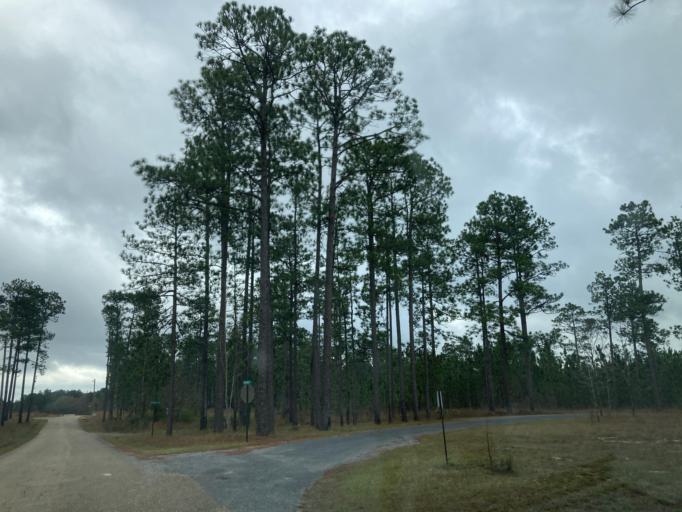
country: US
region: Mississippi
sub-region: Lamar County
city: Lumberton
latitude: 31.0957
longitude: -89.5302
